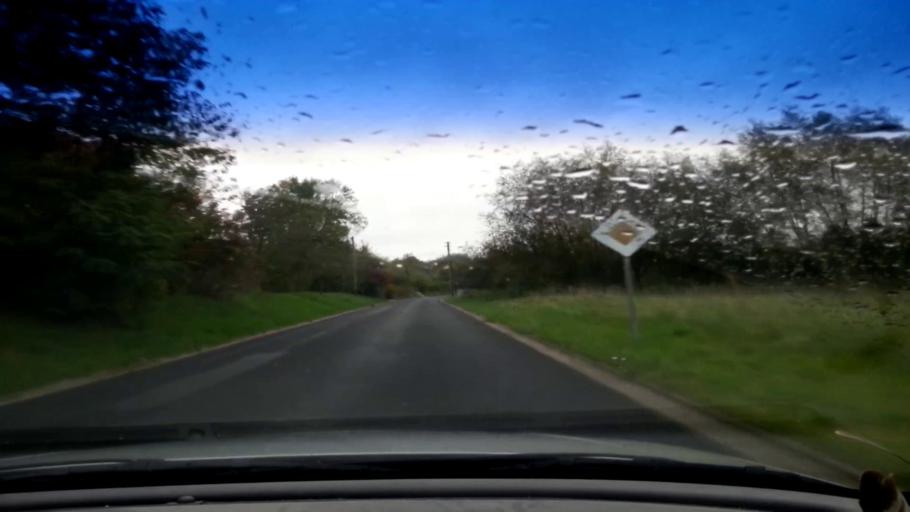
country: DE
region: Bavaria
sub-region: Upper Franconia
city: Priesendorf
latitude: 49.8728
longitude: 10.6995
